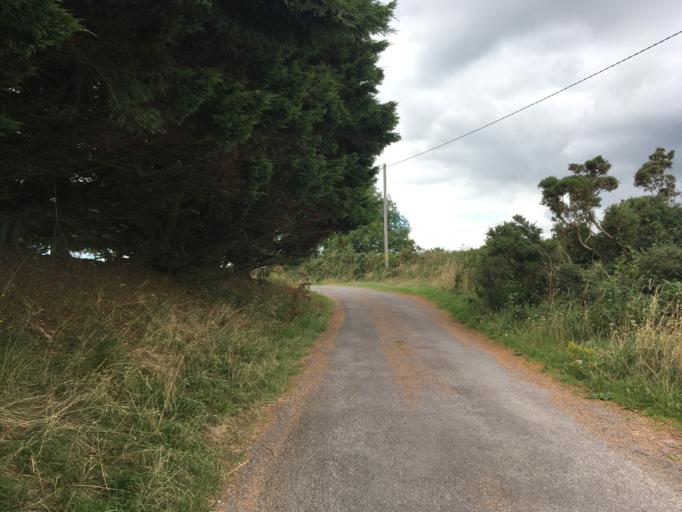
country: IE
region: Munster
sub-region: County Cork
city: Crosshaven
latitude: 51.8076
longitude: -8.2802
